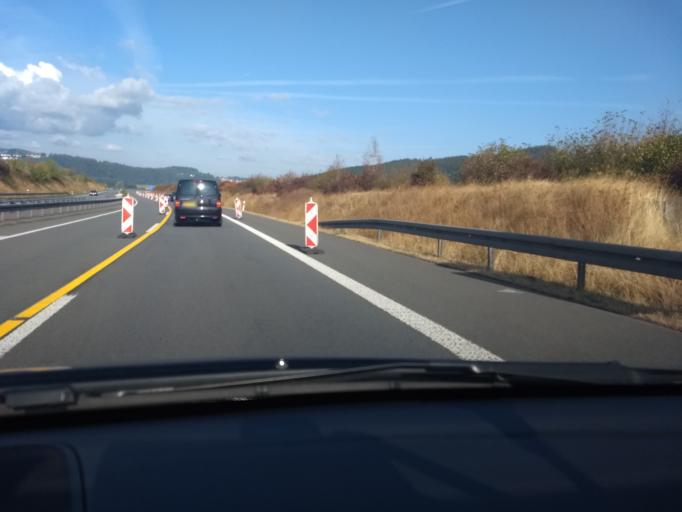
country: DE
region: North Rhine-Westphalia
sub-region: Regierungsbezirk Arnsberg
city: Arnsberg
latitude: 51.3918
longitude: 8.1091
